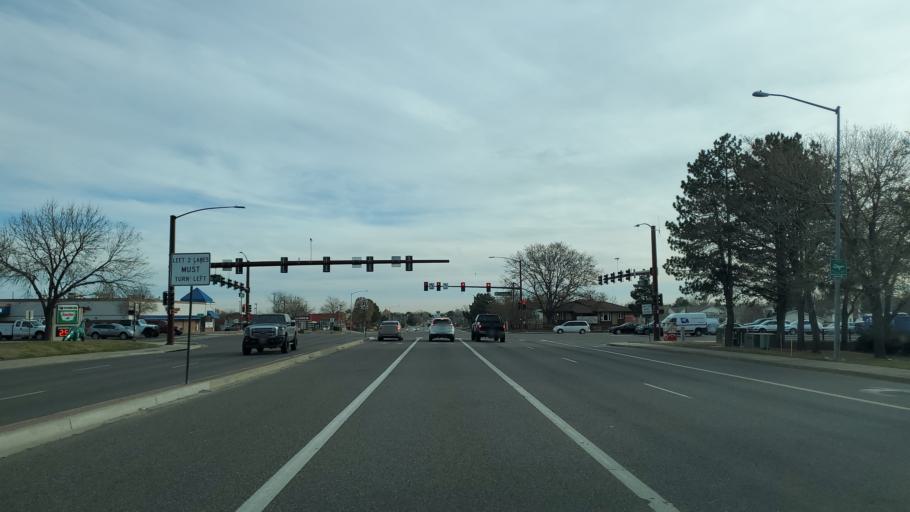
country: US
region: Colorado
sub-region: Adams County
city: Northglenn
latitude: 39.9138
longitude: -104.9412
